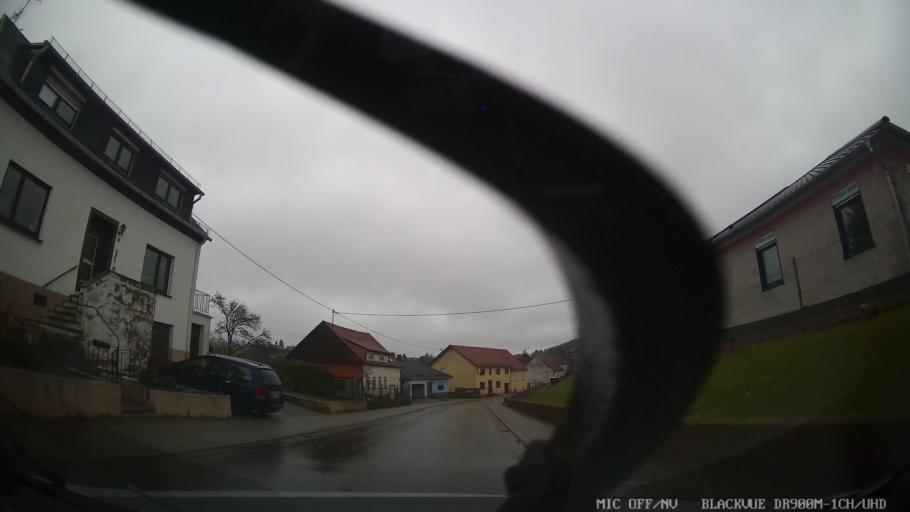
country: DE
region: Rheinland-Pfalz
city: Neuhutten
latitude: 49.5908
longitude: 7.0123
